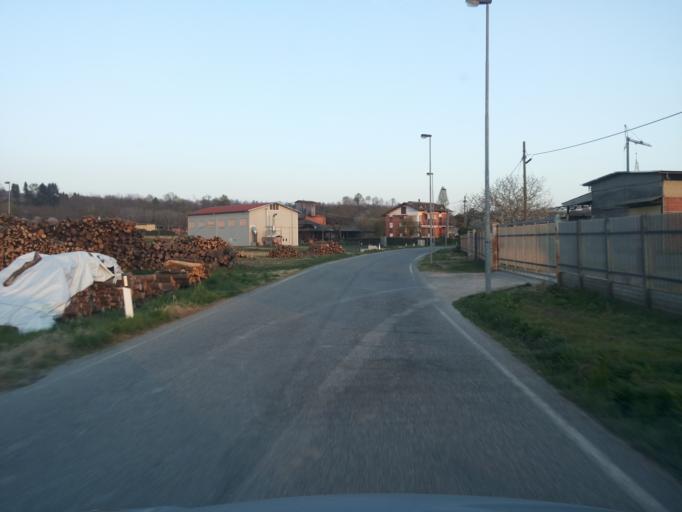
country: IT
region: Piedmont
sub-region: Provincia di Torino
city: Borgomasino
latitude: 45.3583
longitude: 7.9918
